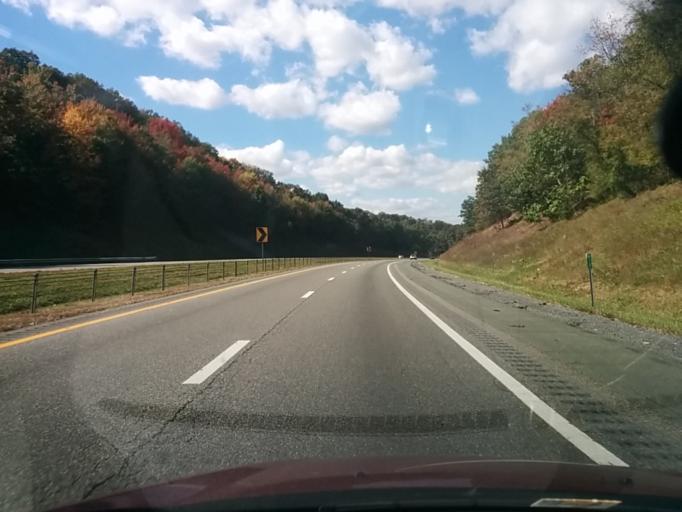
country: US
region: Virginia
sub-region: City of Waynesboro
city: Waynesboro
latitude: 38.0393
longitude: -78.8925
